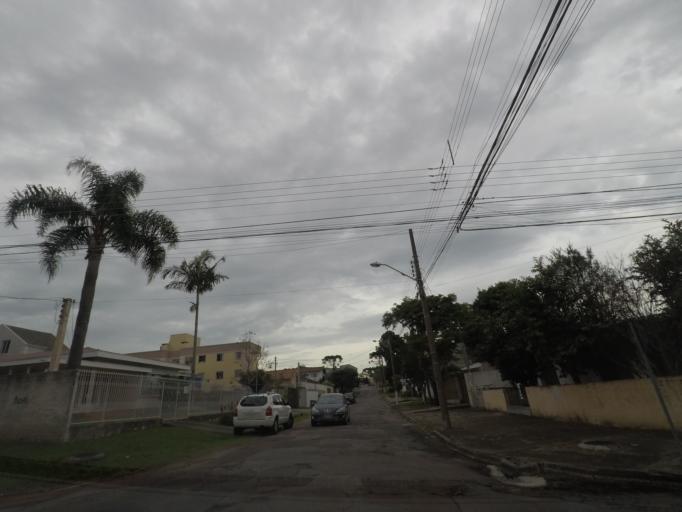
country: BR
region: Parana
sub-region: Curitiba
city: Curitiba
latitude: -25.4715
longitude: -49.3035
